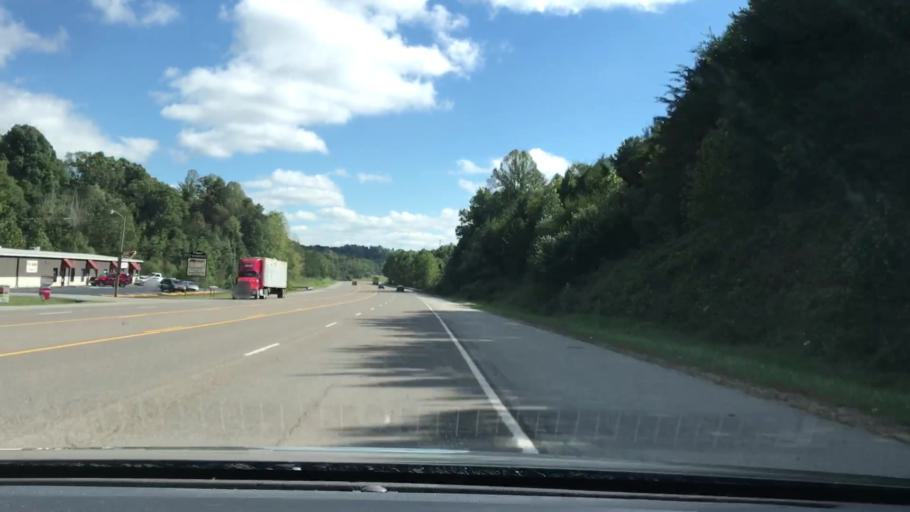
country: US
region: Tennessee
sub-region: Scott County
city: Oneida
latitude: 36.4536
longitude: -84.5452
